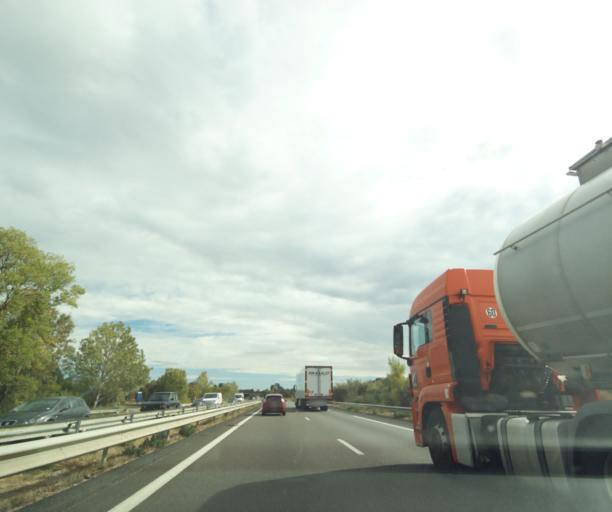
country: FR
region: Languedoc-Roussillon
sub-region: Departement du Gard
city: Caissargues
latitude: 43.7897
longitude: 4.3994
